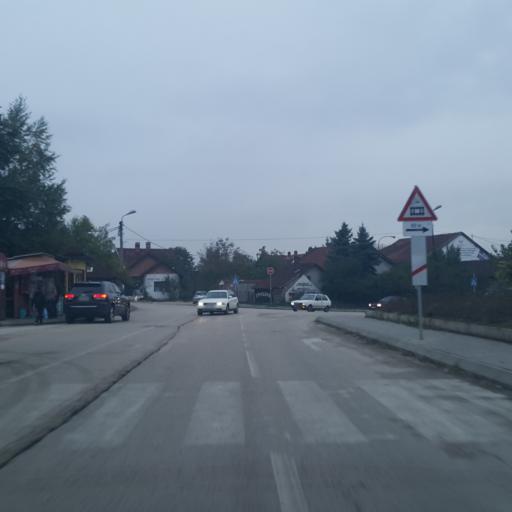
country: RS
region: Central Serbia
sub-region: Zajecarski Okrug
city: Zajecar
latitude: 43.9028
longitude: 22.2649
